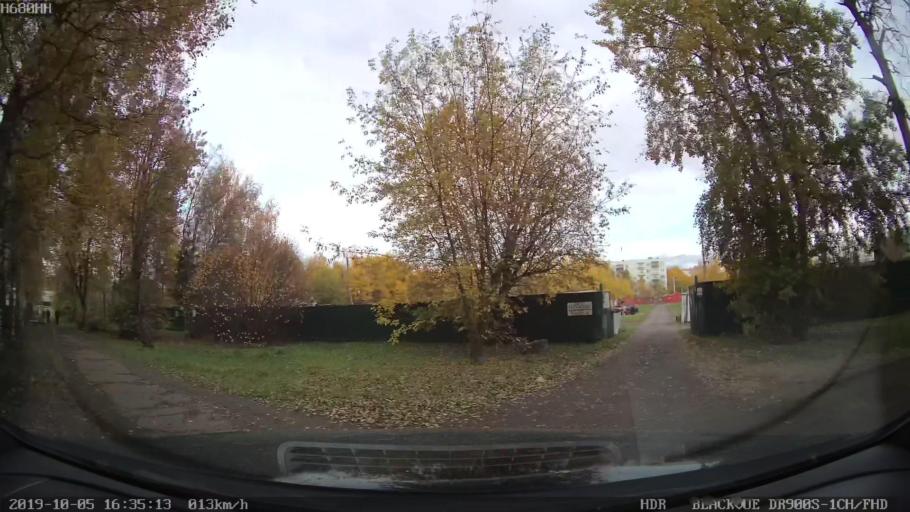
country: RU
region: Moskovskaya
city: Solnechnogorsk
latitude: 56.2190
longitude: 37.0283
